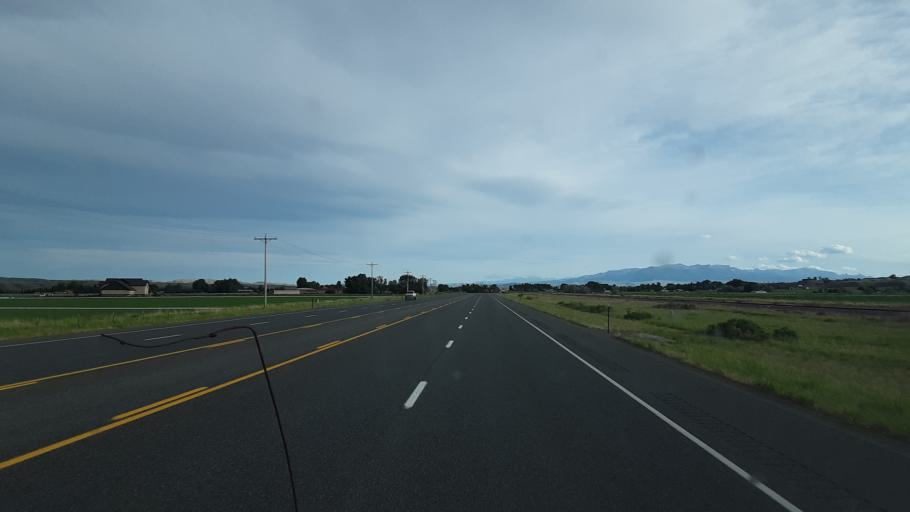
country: US
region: Wyoming
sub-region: Park County
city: Cody
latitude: 44.6070
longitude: -108.9626
